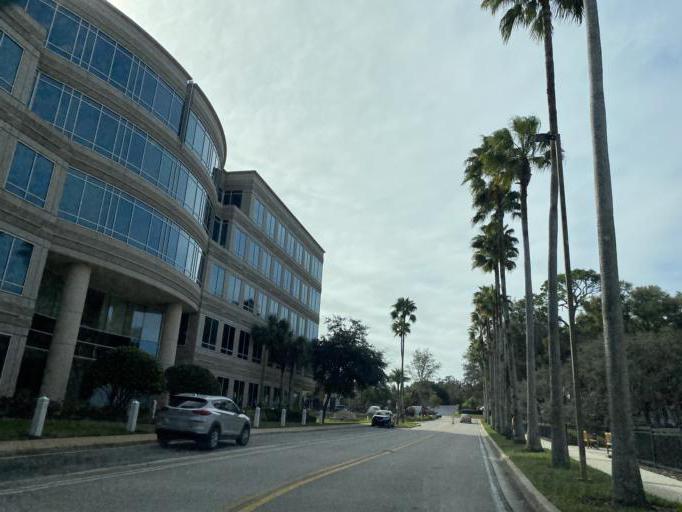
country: US
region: Florida
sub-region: Seminole County
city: Heathrow
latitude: 28.7887
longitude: -81.3530
